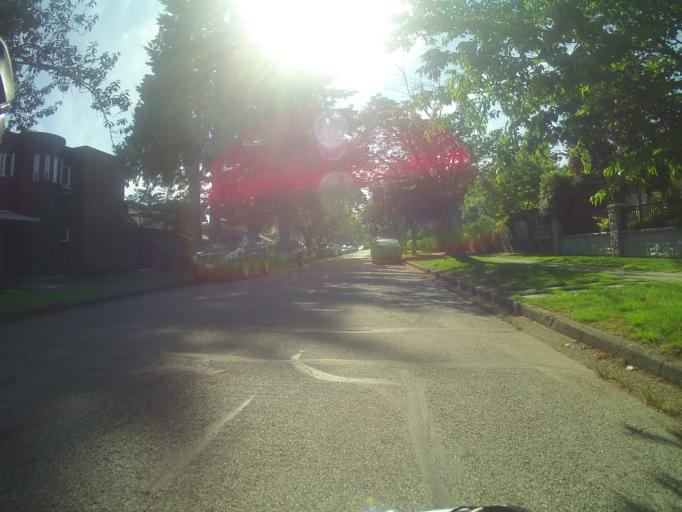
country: CA
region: British Columbia
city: Vancouver
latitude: 49.2173
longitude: -123.1354
